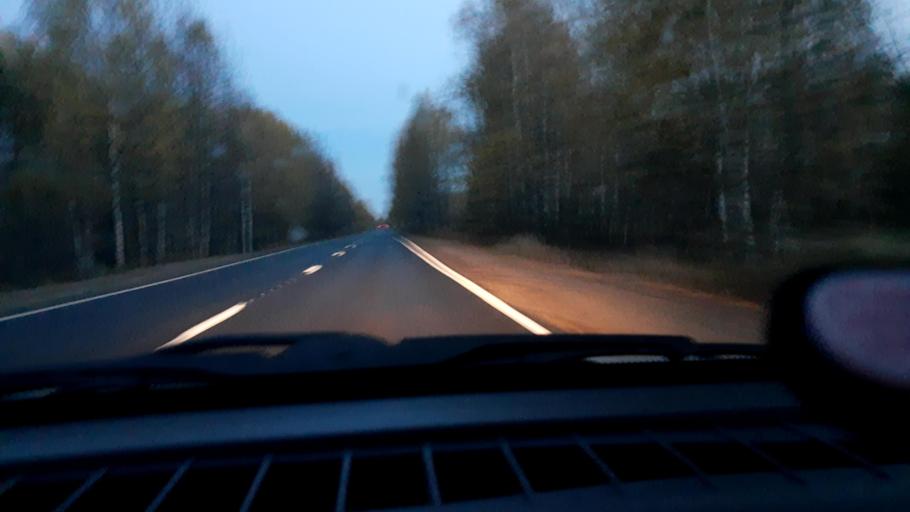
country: RU
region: Nizjnij Novgorod
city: Novaya Balakhna
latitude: 56.5647
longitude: 43.7218
